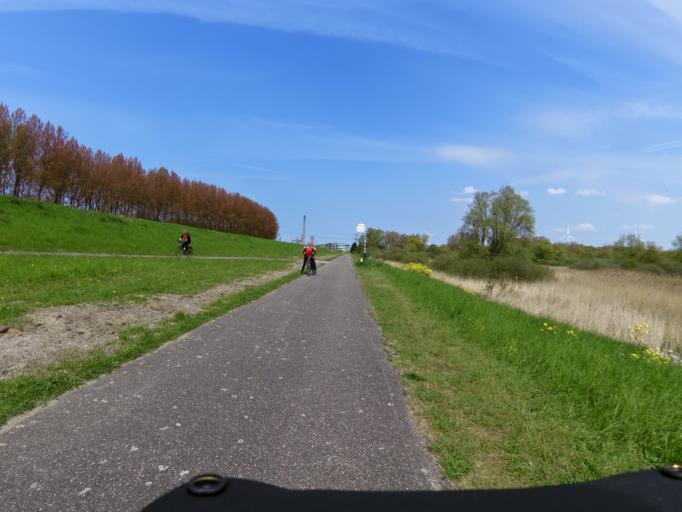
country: NL
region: South Holland
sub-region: Gemeente Rotterdam
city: Hoek van Holland
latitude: 51.9319
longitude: 4.1059
